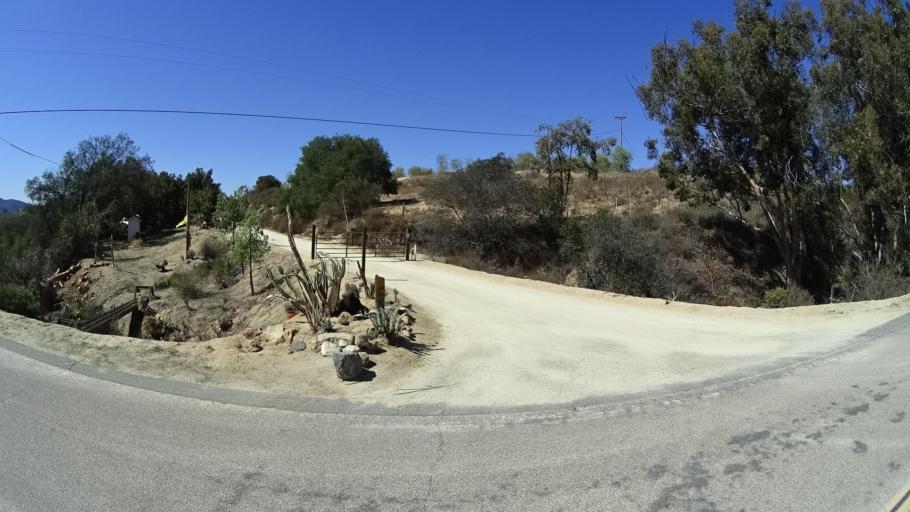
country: US
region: California
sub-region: San Diego County
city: Harbison Canyon
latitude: 32.7883
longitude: -116.8077
